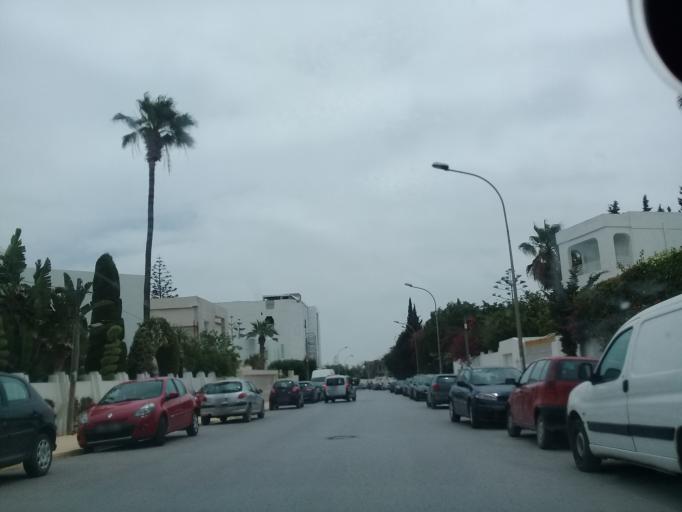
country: TN
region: Tunis
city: Tunis
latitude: 36.8428
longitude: 10.1615
